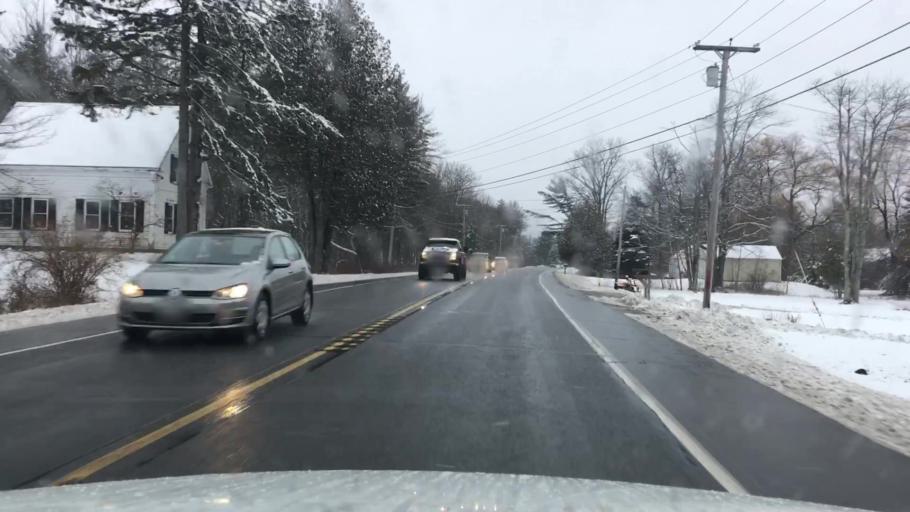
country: US
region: Maine
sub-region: Knox County
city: Rockport
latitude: 44.1746
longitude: -69.1235
